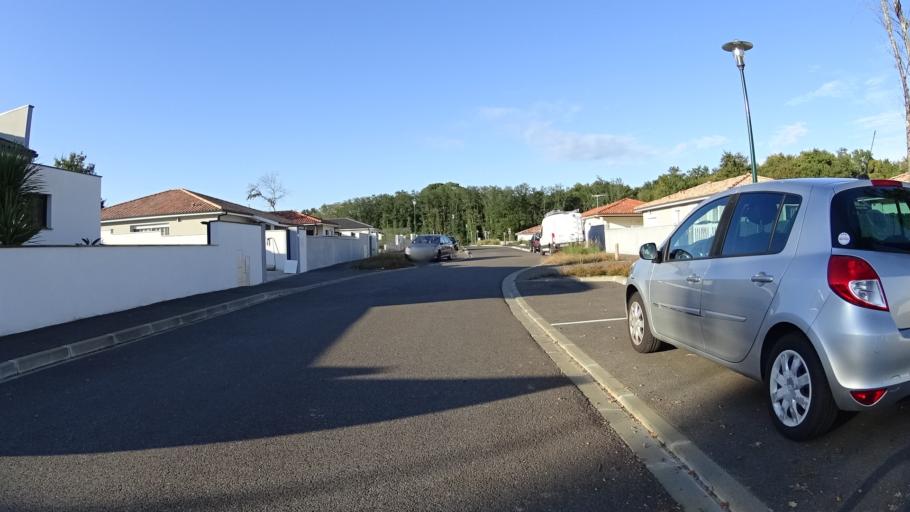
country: FR
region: Aquitaine
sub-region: Departement des Landes
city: Saint-Paul-les-Dax
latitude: 43.7403
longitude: -1.0460
